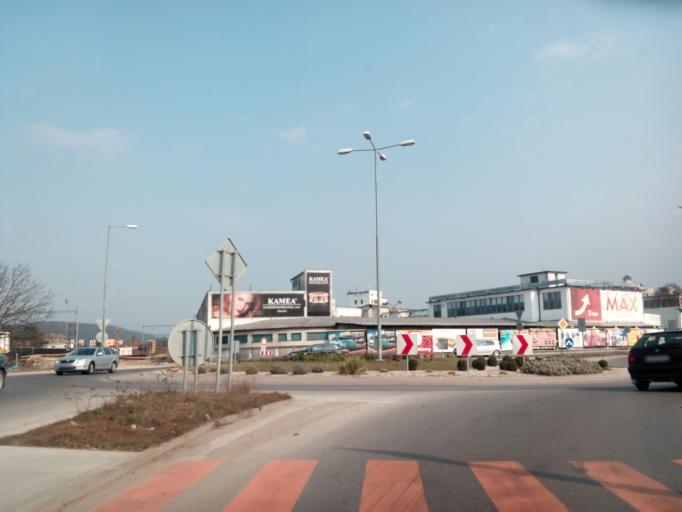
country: SK
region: Trenciansky
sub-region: Okres Trencin
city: Trencin
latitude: 48.9000
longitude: 18.0283
